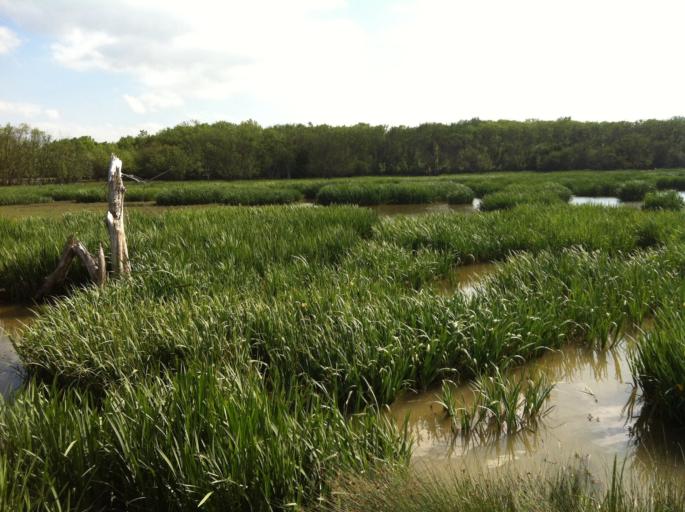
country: ES
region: Basque Country
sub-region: Provincia de Alava
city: Gasteiz / Vitoria
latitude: 42.8583
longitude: -2.6333
